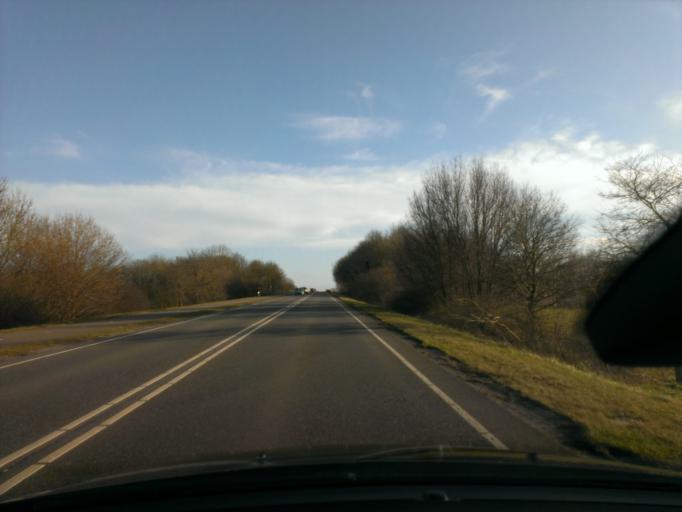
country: NL
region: Gelderland
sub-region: Gemeente Voorst
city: Twello
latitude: 52.2095
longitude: 6.0833
